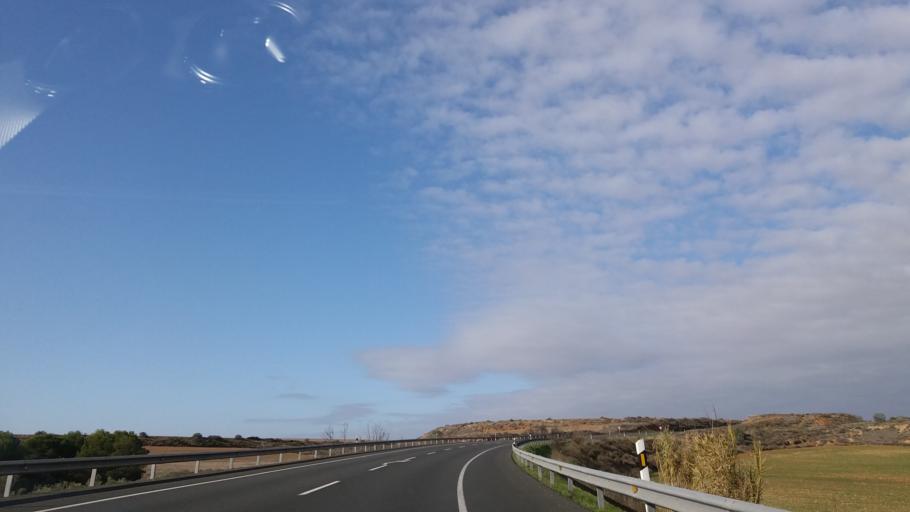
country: ES
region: Aragon
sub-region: Provincia de Huesca
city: Candasnos
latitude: 41.5148
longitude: 0.1472
